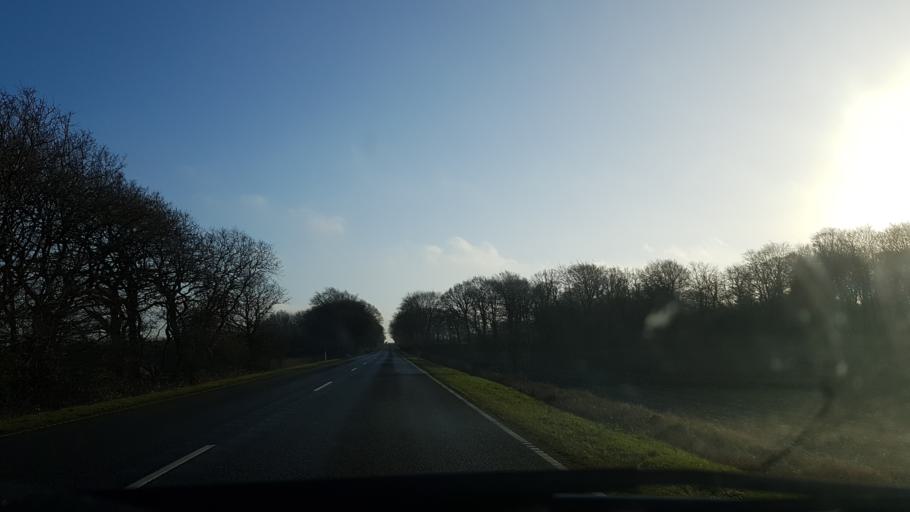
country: DK
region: South Denmark
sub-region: Tonder Kommune
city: Toftlund
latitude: 55.2241
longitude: 9.1757
